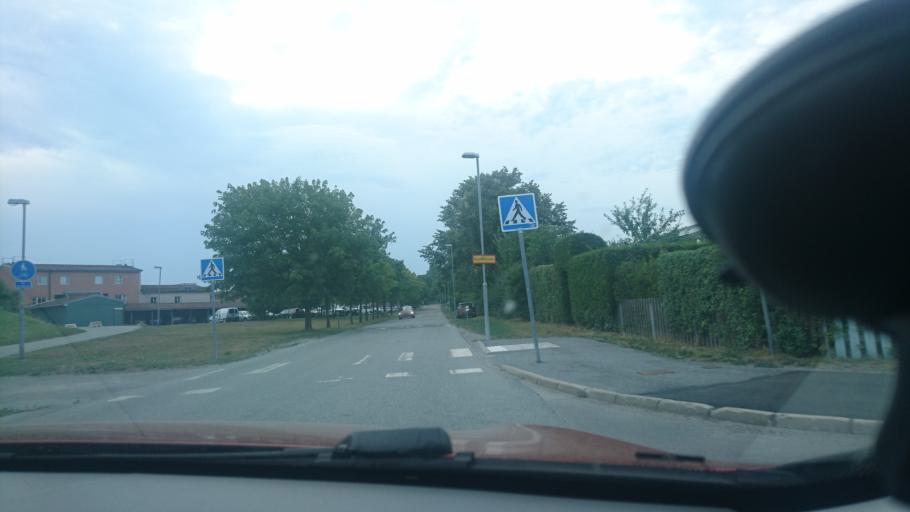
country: SE
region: Stockholm
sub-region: Upplands Vasby Kommun
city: Upplands Vaesby
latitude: 59.5052
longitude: 17.9143
